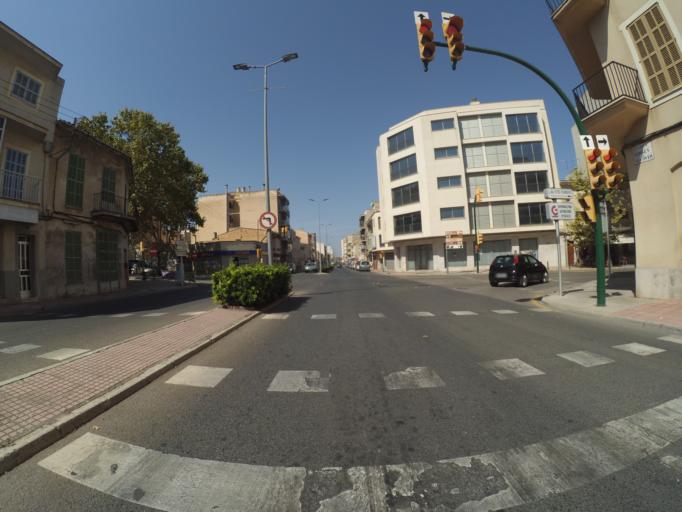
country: ES
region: Balearic Islands
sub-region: Illes Balears
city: Manacor
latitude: 39.5661
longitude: 3.2063
